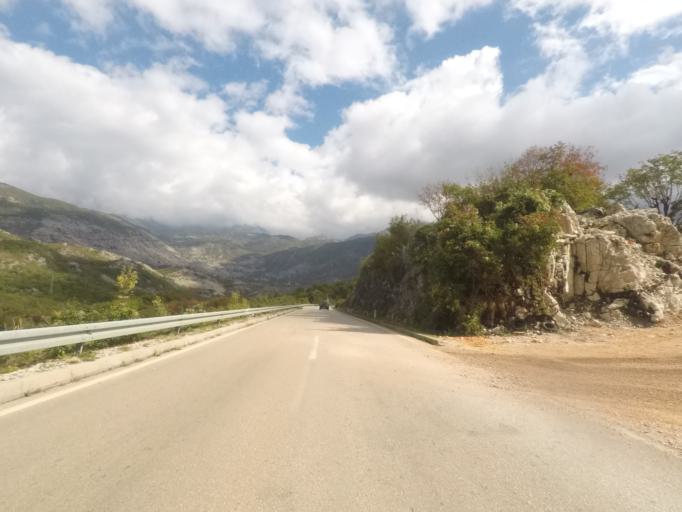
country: ME
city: Igalo
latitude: 42.5264
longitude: 18.4708
